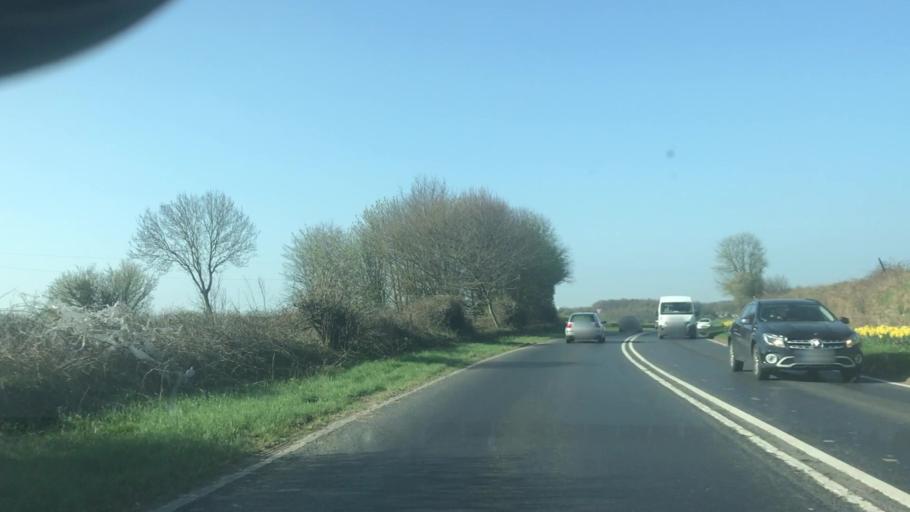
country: GB
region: England
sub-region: City and Borough of Leeds
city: Shadwell
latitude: 53.8772
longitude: -1.5090
